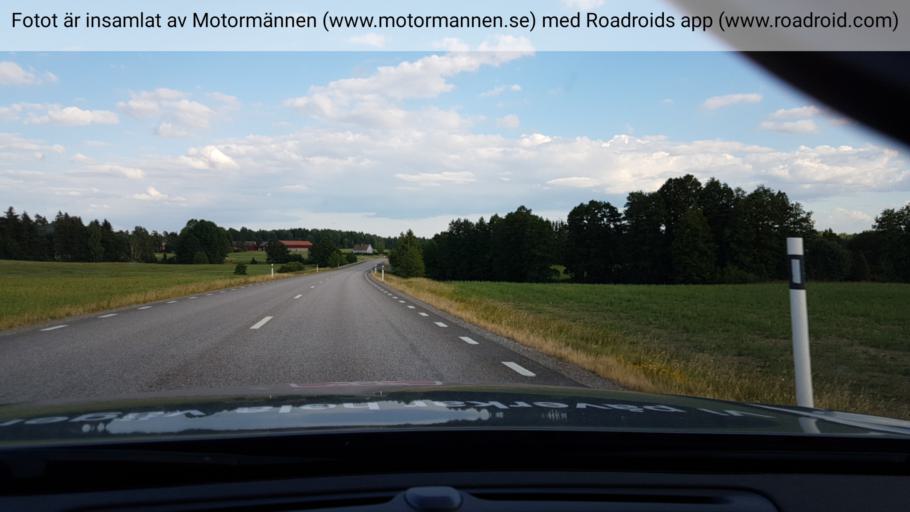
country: SE
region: Uppsala
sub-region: Heby Kommun
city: Morgongava
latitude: 59.8831
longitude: 16.9166
